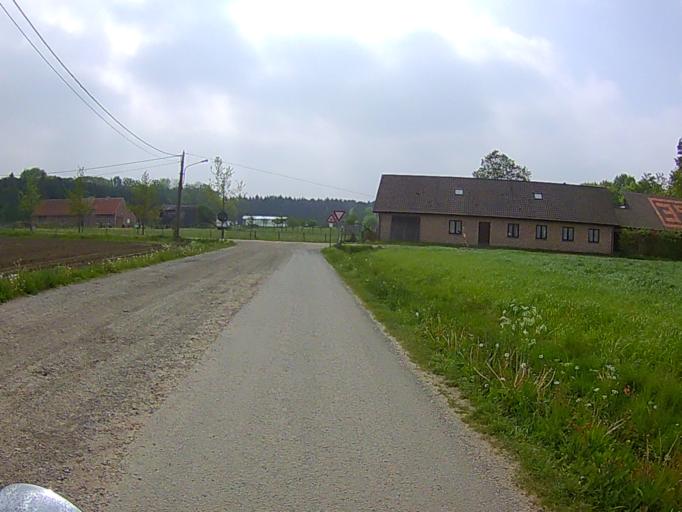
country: BE
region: Flanders
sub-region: Provincie Antwerpen
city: Grobbendonk
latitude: 51.2073
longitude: 4.7246
